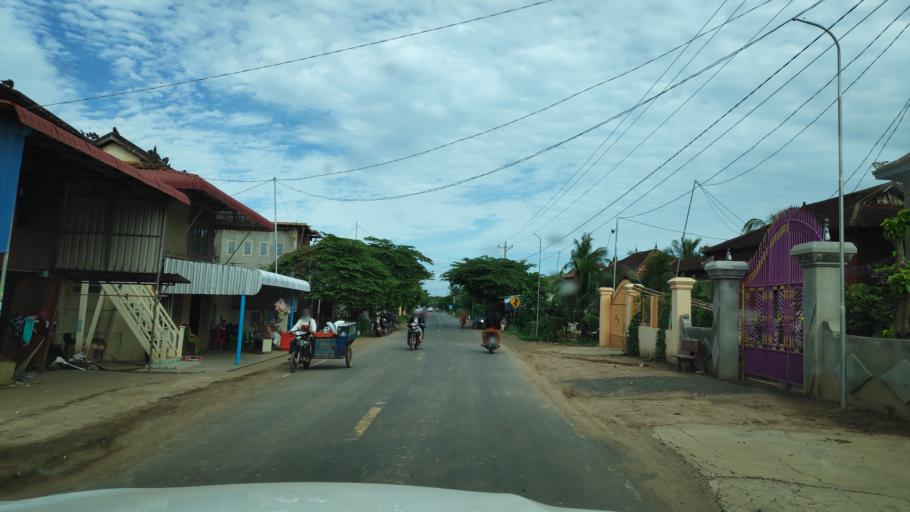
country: KH
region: Kampong Cham
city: Kampong Cham
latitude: 11.9474
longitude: 105.2420
